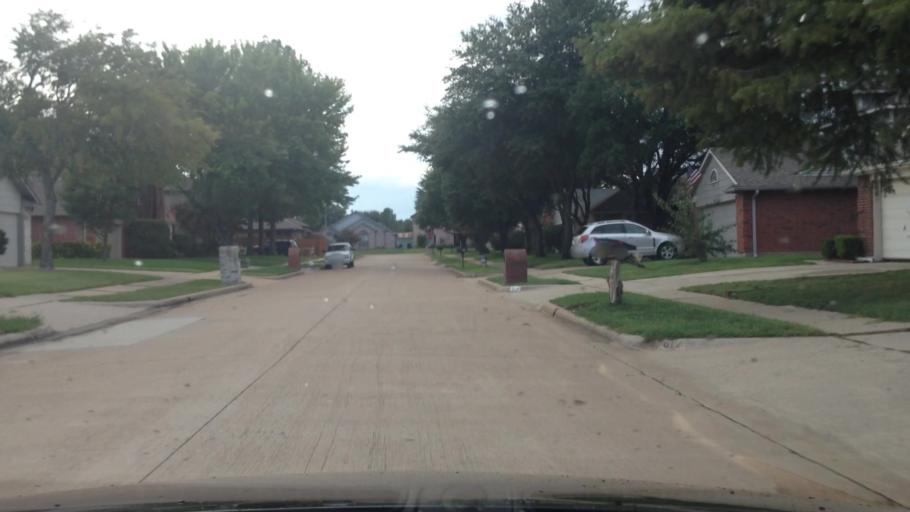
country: US
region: Texas
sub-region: Denton County
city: Flower Mound
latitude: 33.0166
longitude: -97.0419
